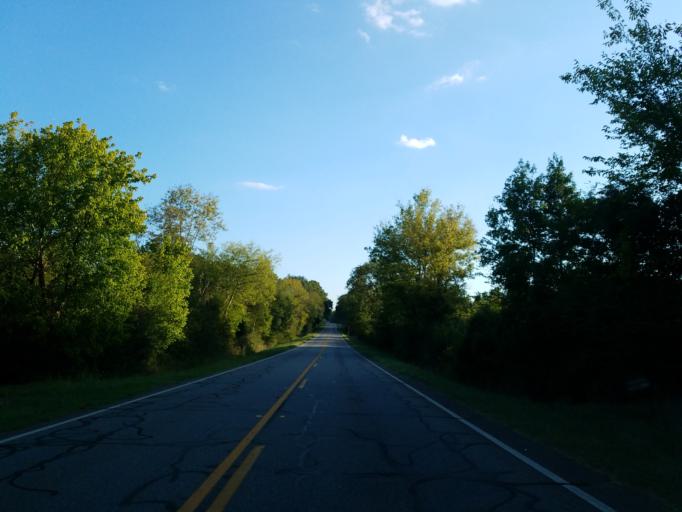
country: US
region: Georgia
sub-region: Murray County
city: Chatsworth
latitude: 34.5628
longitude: -84.7079
